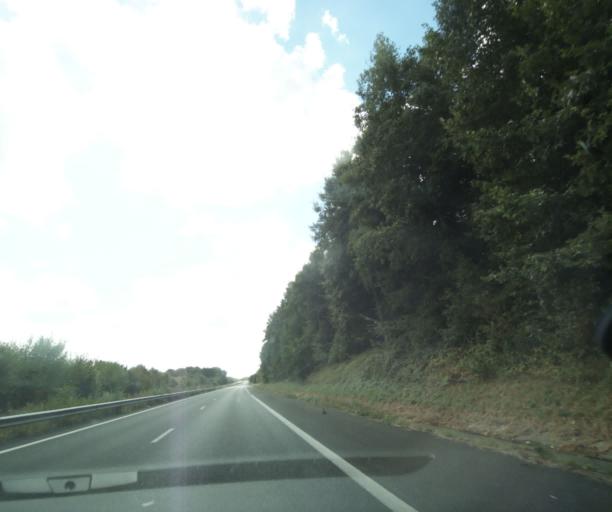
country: FR
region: Poitou-Charentes
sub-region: Departement de la Charente-Maritime
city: Cabariot
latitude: 45.9361
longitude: -0.8416
